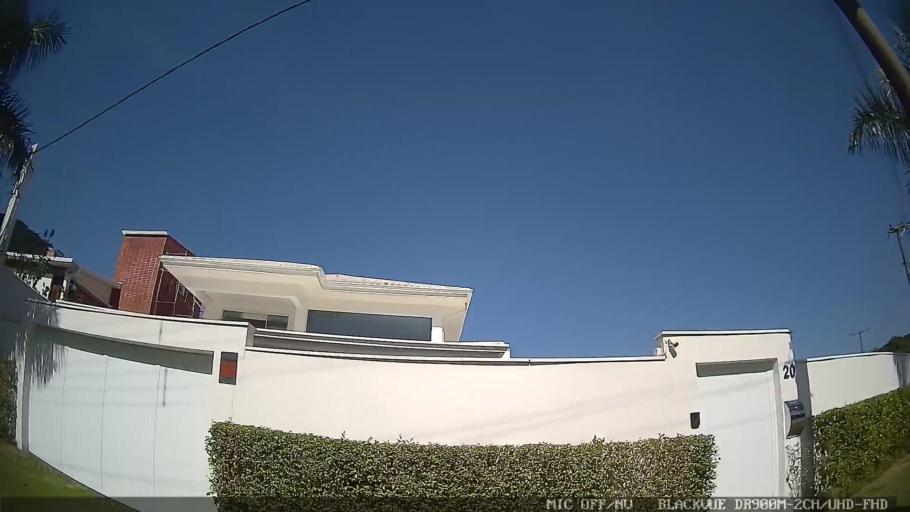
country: BR
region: Sao Paulo
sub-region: Guaruja
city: Guaruja
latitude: -24.0174
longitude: -46.2903
